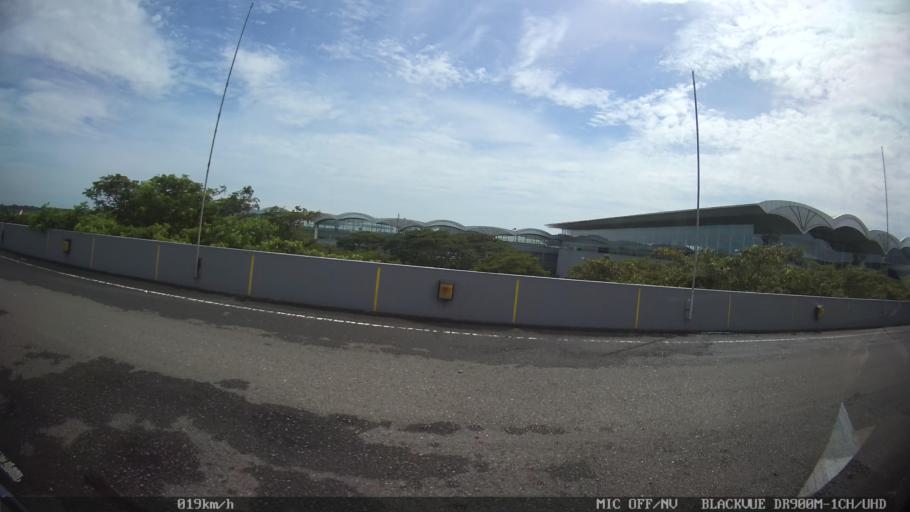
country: ID
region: North Sumatra
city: Percut
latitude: 3.6359
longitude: 98.8779
